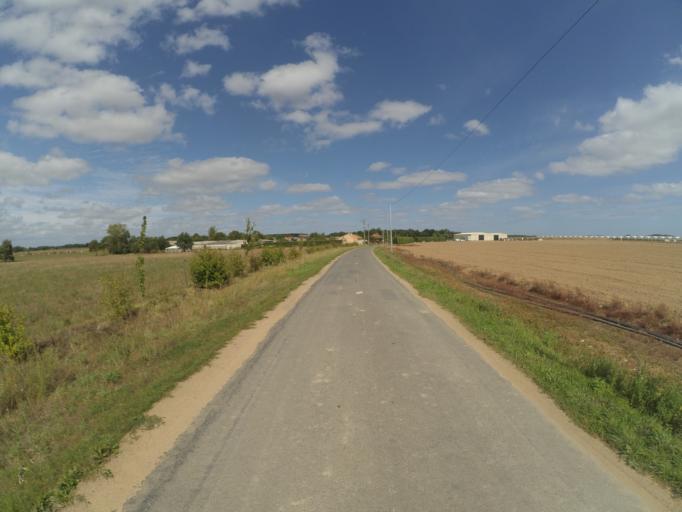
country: FR
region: Pays de la Loire
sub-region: Departement de la Loire-Atlantique
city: La Planche
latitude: 47.0287
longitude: -1.4574
